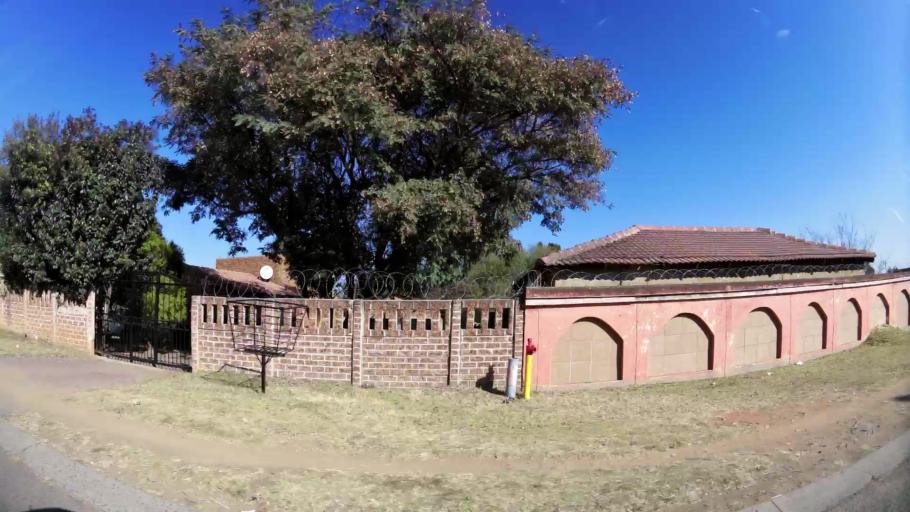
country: ZA
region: Gauteng
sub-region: City of Johannesburg Metropolitan Municipality
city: Modderfontein
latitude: -26.0496
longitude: 28.1959
